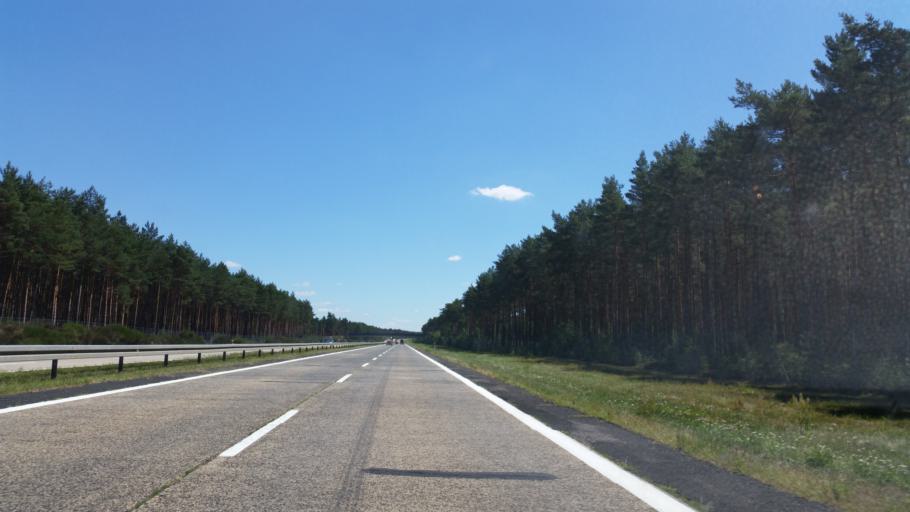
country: PL
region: Lubusz
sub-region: Powiat zaganski
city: Malomice
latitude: 51.4221
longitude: 15.4582
